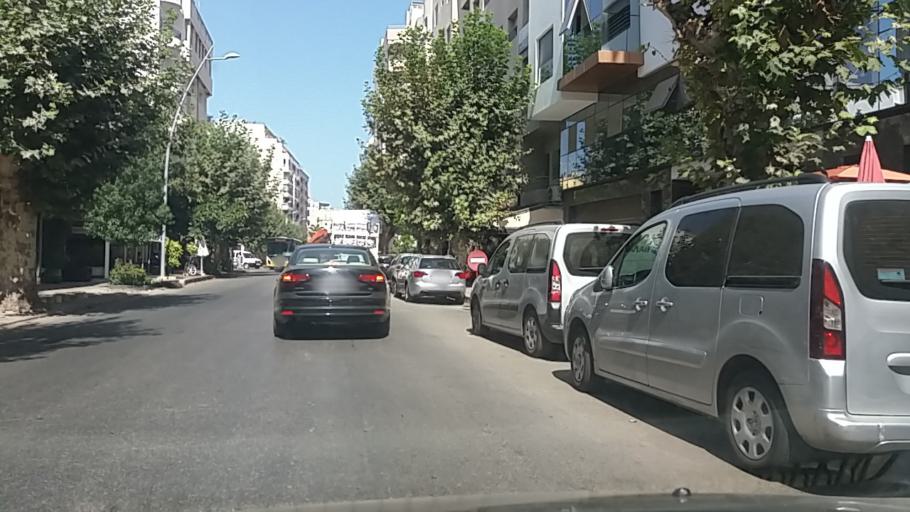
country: MA
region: Gharb-Chrarda-Beni Hssen
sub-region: Kenitra Province
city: Kenitra
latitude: 34.2574
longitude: -6.5840
